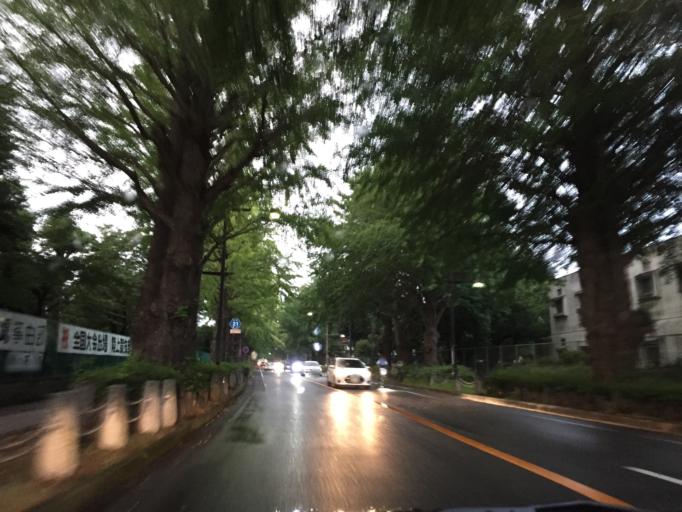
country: JP
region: Shizuoka
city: Mishima
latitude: 35.1296
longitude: 138.9144
